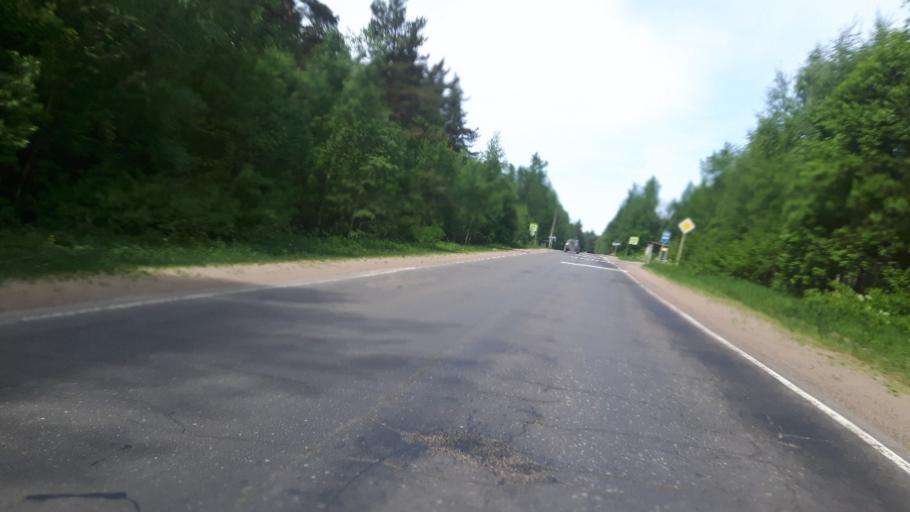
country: RU
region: Leningrad
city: Ust'-Luga
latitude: 59.6447
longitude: 28.2698
